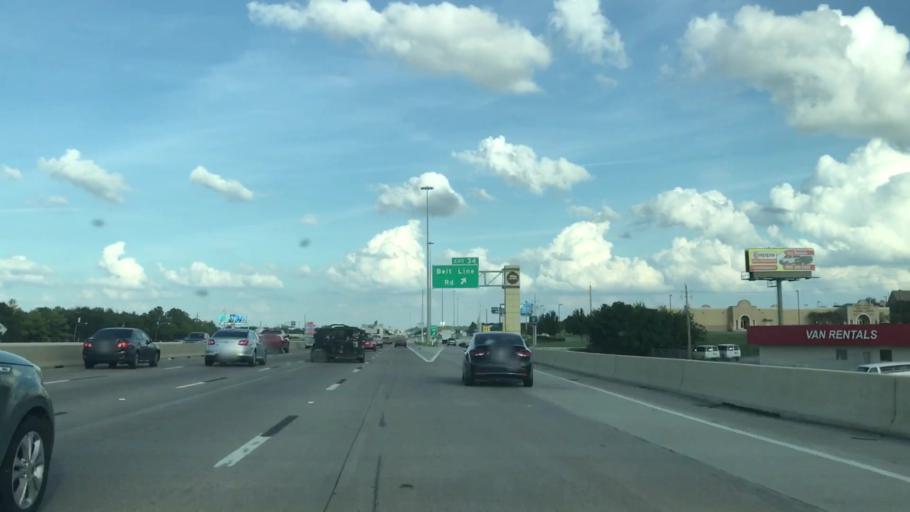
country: US
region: Texas
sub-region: Dallas County
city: Grand Prairie
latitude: 32.7593
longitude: -97.0112
